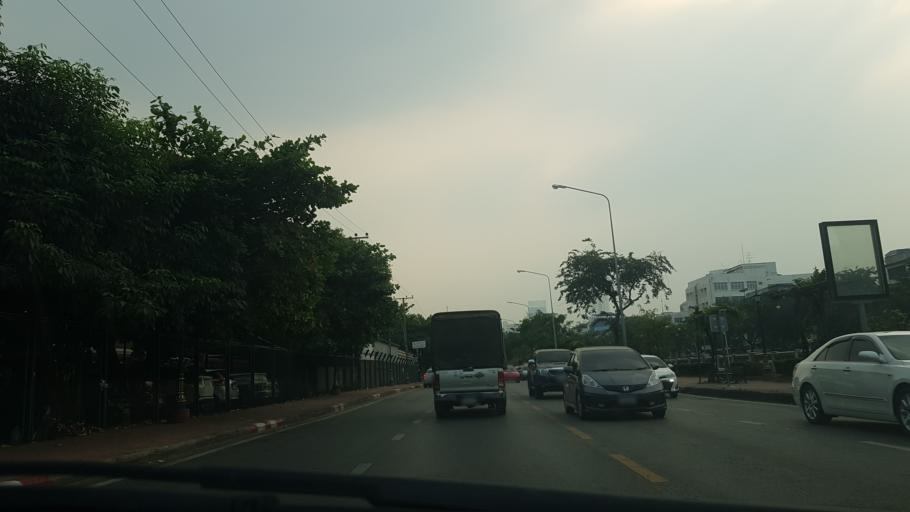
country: TH
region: Bangkok
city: Pathum Wan
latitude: 13.7444
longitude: 100.5164
